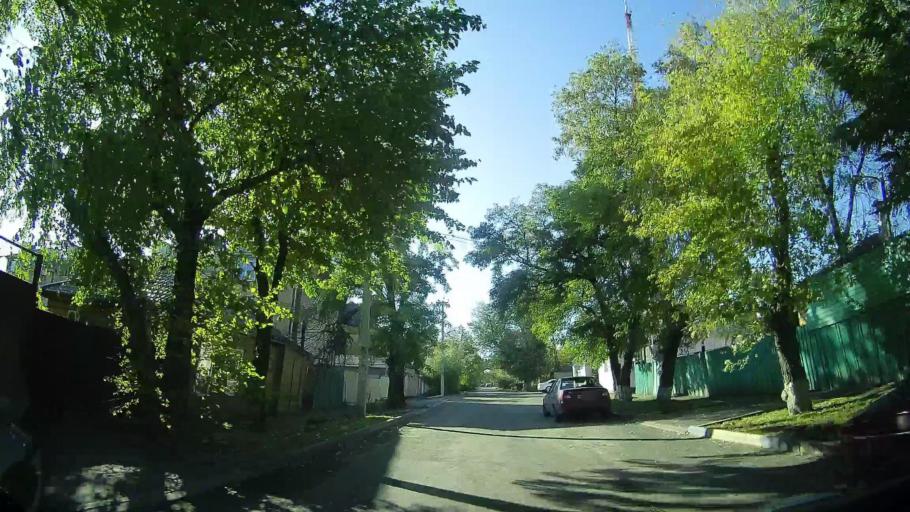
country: RU
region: Rostov
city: Rostov-na-Donu
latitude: 47.2131
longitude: 39.6813
